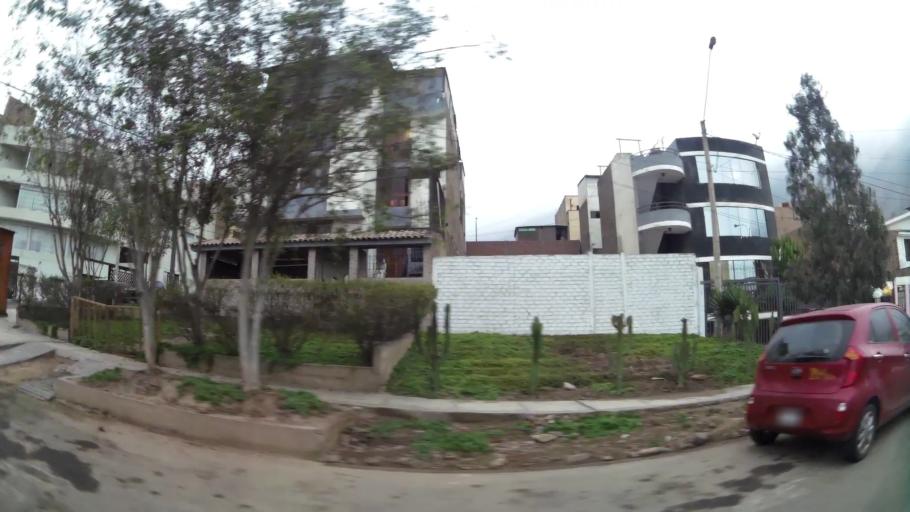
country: PE
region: Lima
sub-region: Lima
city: La Molina
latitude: -12.1140
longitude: -76.9376
